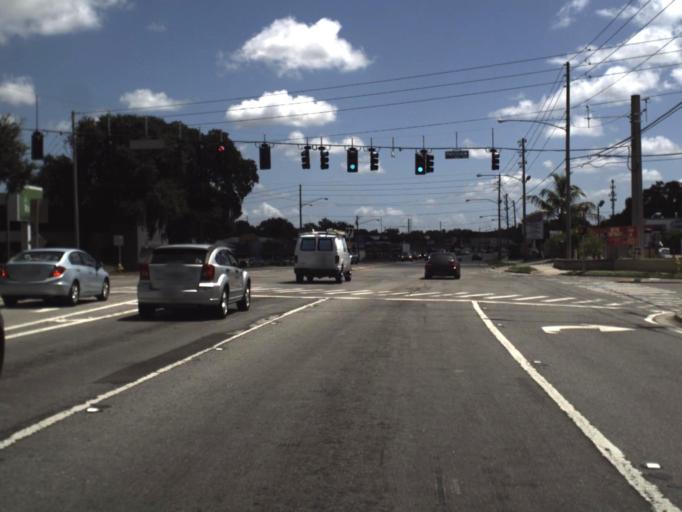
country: US
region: Florida
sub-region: Pinellas County
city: Dunedin
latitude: 28.0184
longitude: -82.7761
